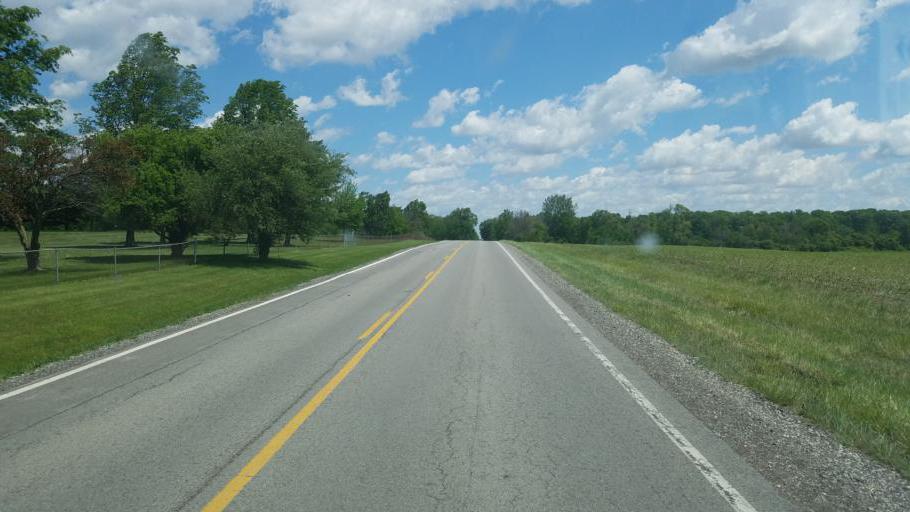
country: US
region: Ohio
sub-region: Huron County
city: Plymouth
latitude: 40.9384
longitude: -82.7257
